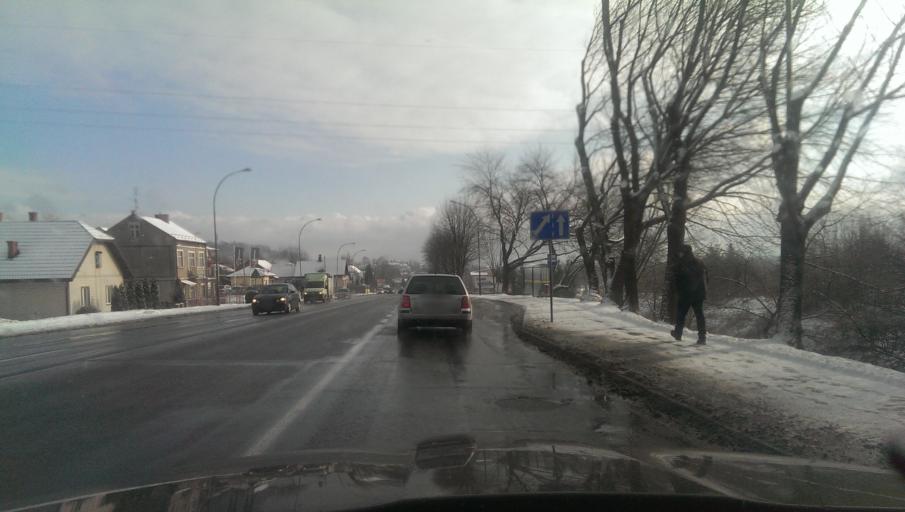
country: PL
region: Subcarpathian Voivodeship
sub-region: Powiat sanocki
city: Sanok
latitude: 49.5639
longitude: 22.1818
